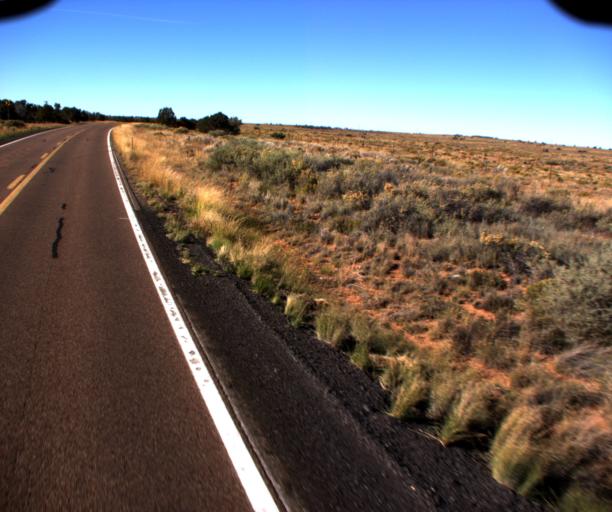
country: US
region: Arizona
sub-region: Navajo County
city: Holbrook
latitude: 34.6814
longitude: -110.3108
